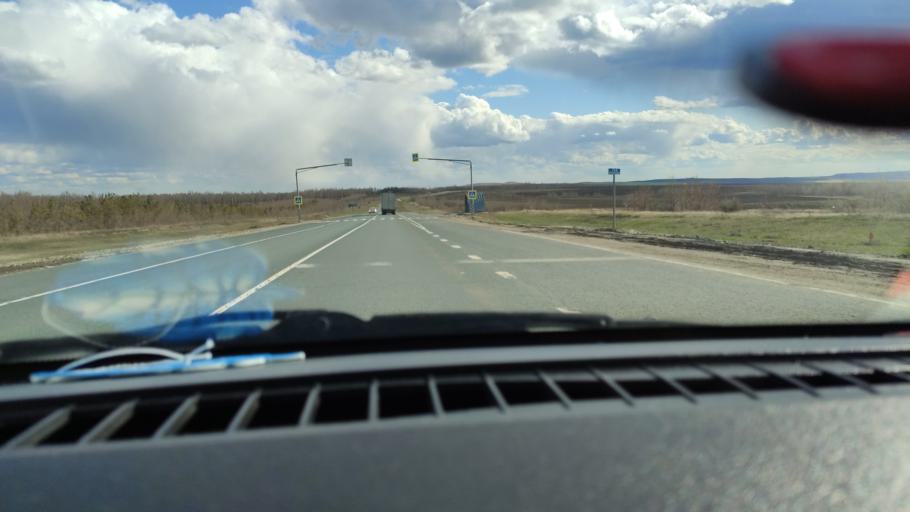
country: RU
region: Saratov
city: Alekseyevka
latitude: 52.2858
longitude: 47.9313
